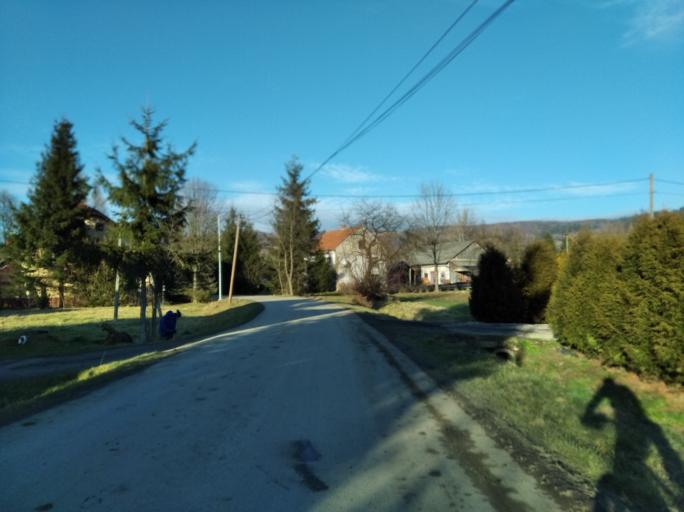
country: PL
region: Subcarpathian Voivodeship
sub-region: Powiat strzyzowski
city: Strzyzow
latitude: 49.8343
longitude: 21.8353
